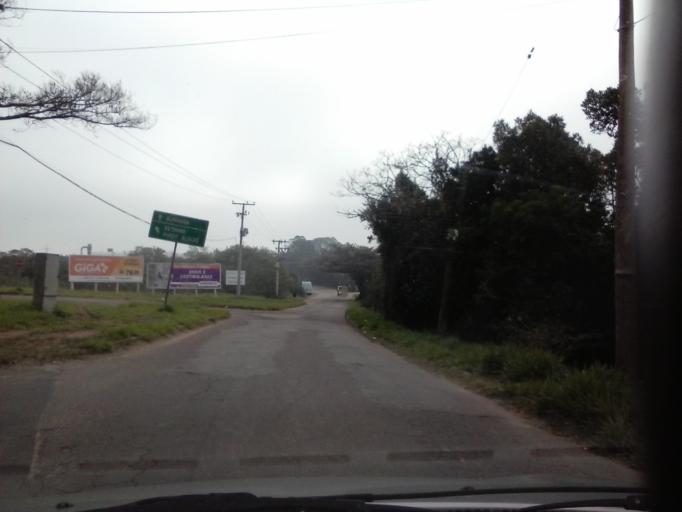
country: BR
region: Rio Grande do Sul
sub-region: Viamao
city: Viamao
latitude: -30.0744
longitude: -51.0449
